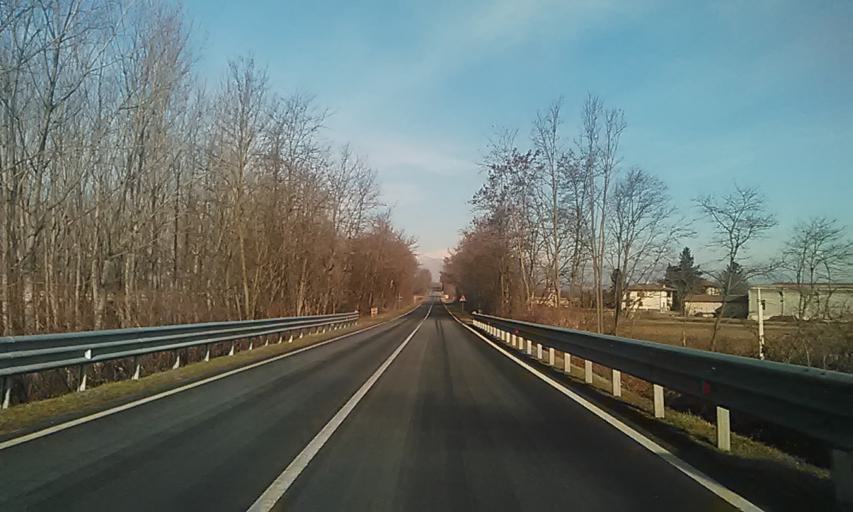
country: IT
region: Piedmont
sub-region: Provincia di Vercelli
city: Formigliana
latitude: 45.4355
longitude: 8.2962
